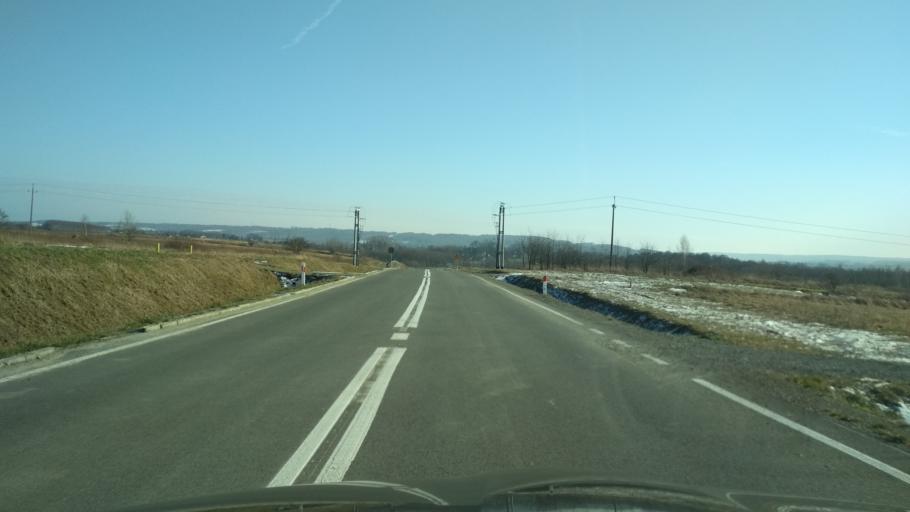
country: PL
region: Subcarpathian Voivodeship
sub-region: Powiat ropczycko-sedziszowski
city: Sedziszow Malopolski
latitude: 50.0777
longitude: 21.7247
